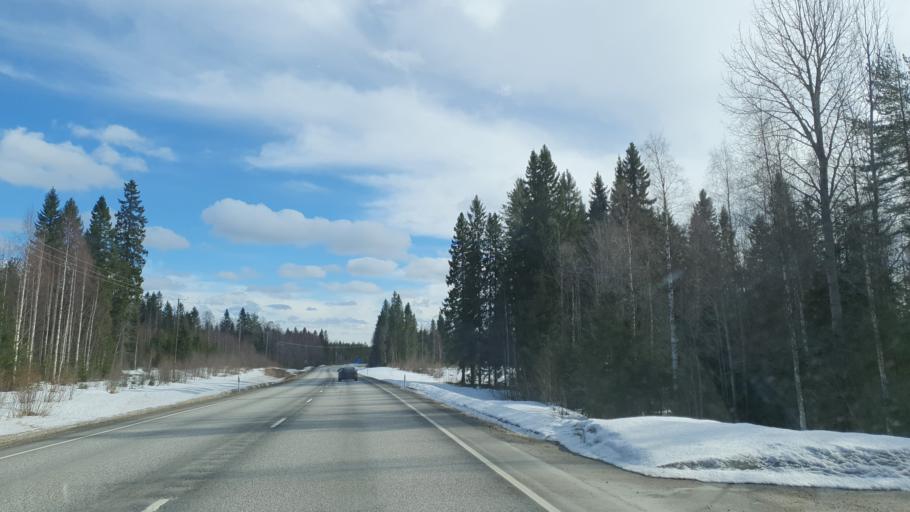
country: FI
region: Kainuu
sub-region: Kajaani
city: Paltamo
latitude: 64.3841
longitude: 28.0086
